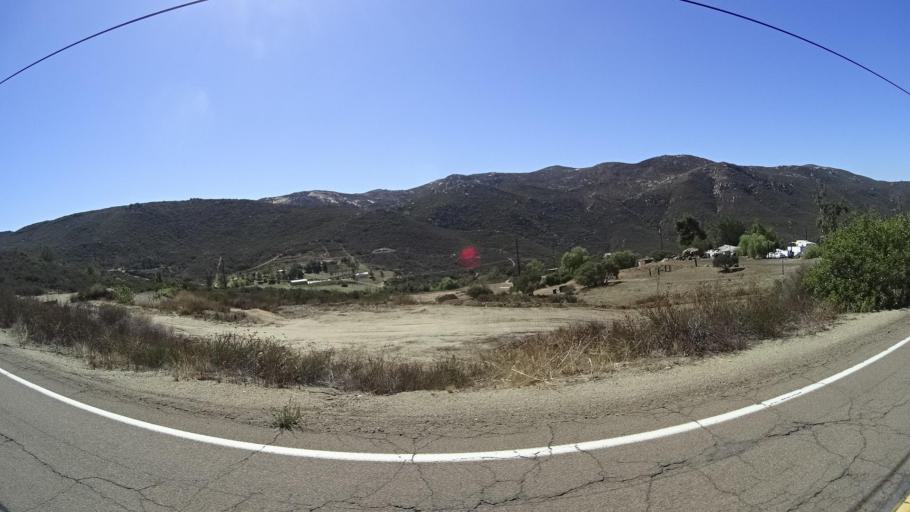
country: US
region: California
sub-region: San Diego County
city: Alpine
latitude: 32.7873
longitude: -116.7254
